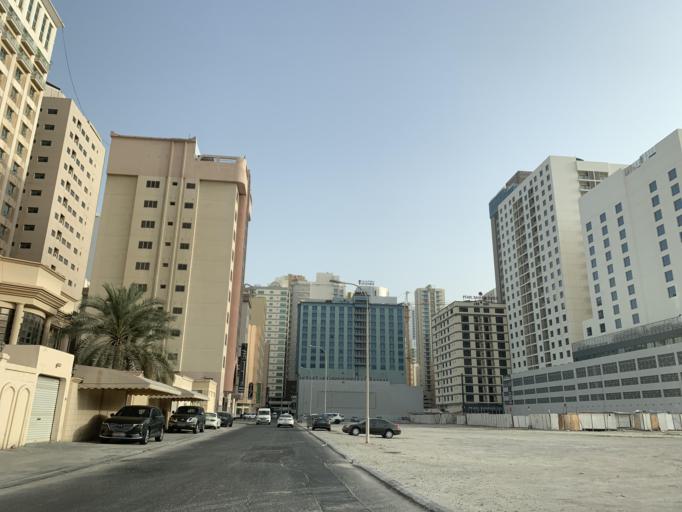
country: BH
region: Manama
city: Manama
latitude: 26.2173
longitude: 50.6060
